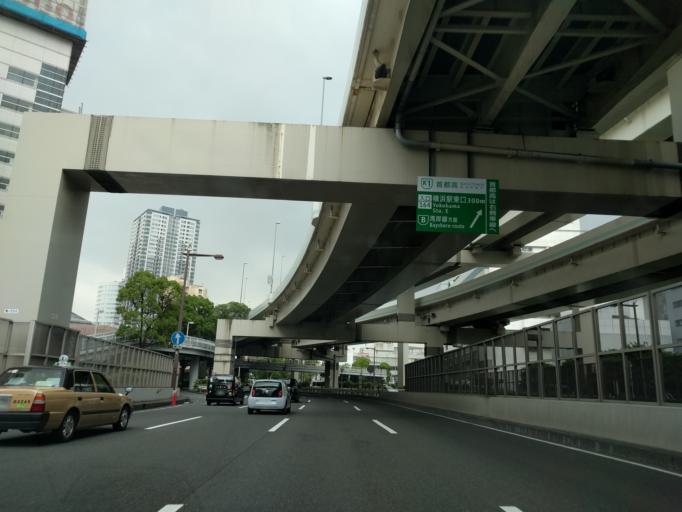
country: JP
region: Kanagawa
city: Yokohama
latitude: 35.4663
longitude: 139.6245
